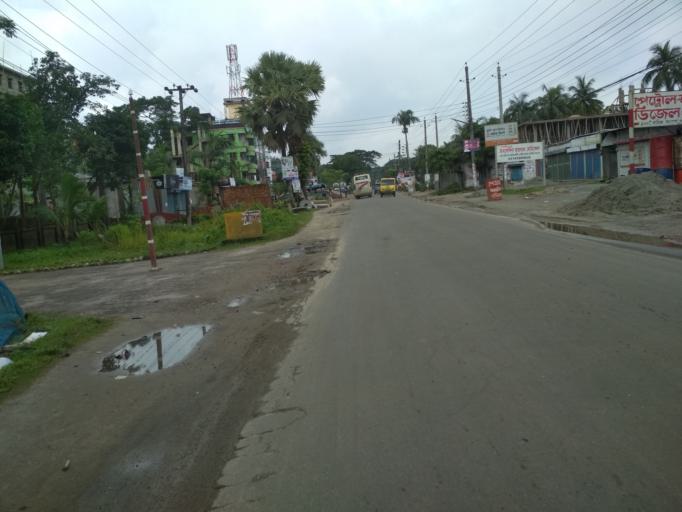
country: BD
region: Chittagong
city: Lakshmipur
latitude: 22.9452
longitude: 90.8245
